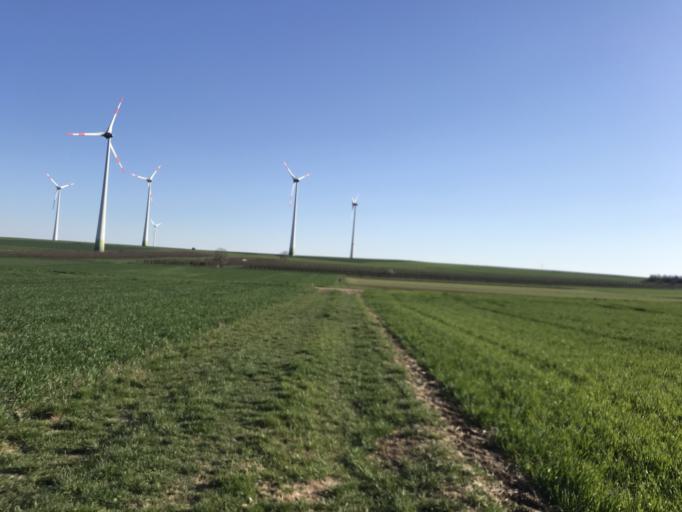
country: DE
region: Rheinland-Pfalz
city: Klein-Winternheim
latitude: 49.9468
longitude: 8.2347
